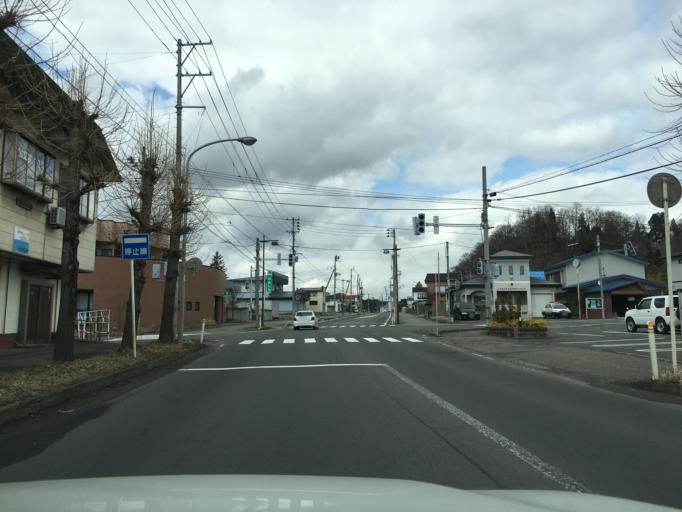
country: JP
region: Akita
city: Hanawa
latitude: 40.2672
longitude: 140.7694
